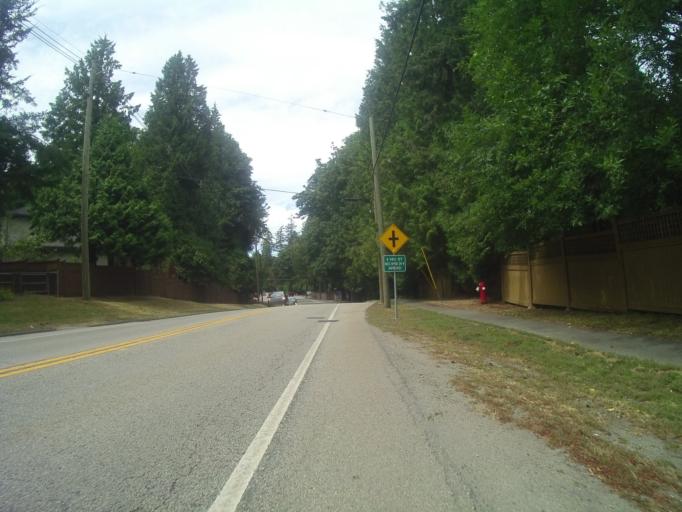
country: CA
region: British Columbia
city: Surrey
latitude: 49.0675
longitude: -122.8319
